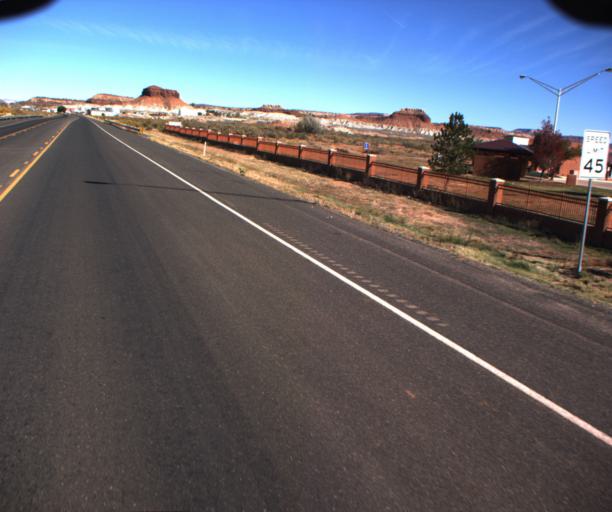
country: US
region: Arizona
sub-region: Coconino County
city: Fredonia
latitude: 36.9624
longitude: -112.5269
